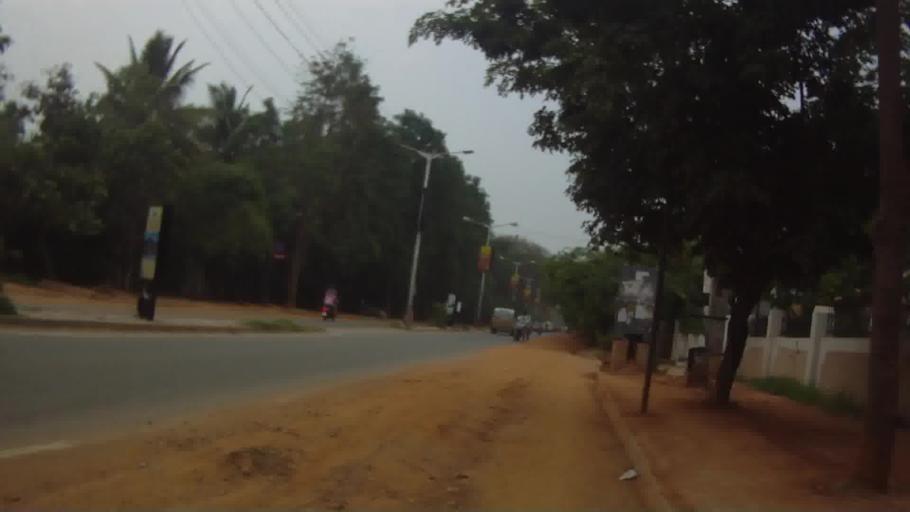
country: IN
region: Karnataka
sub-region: Bangalore Rural
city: Hoskote
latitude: 12.9570
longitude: 77.7361
